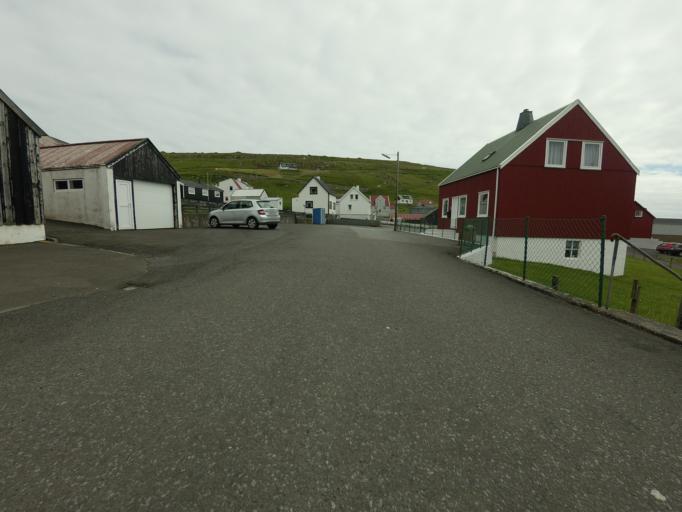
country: FO
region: Suduroy
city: Vagur
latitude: 61.4035
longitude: -6.7124
